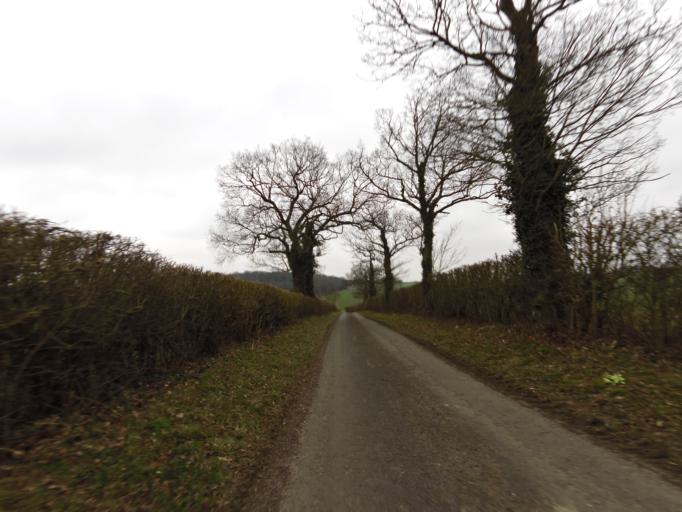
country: GB
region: England
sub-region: Suffolk
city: Framlingham
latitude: 52.2408
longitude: 1.3901
